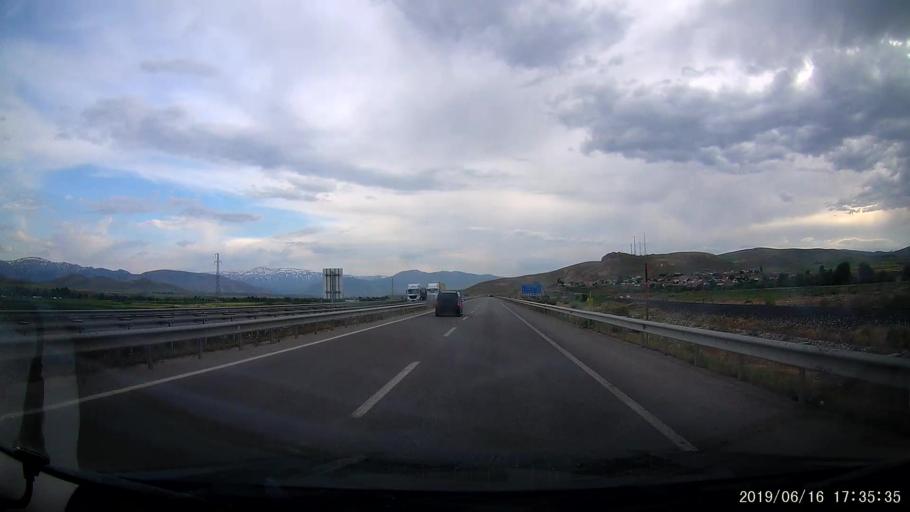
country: TR
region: Erzincan
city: Tercan
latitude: 39.7357
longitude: 40.2618
